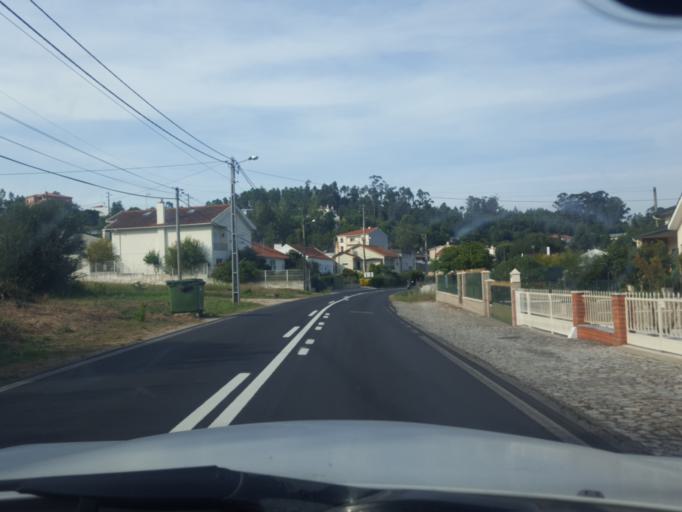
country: PT
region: Leiria
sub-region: Leiria
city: Leiria
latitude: 39.7075
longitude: -8.7929
